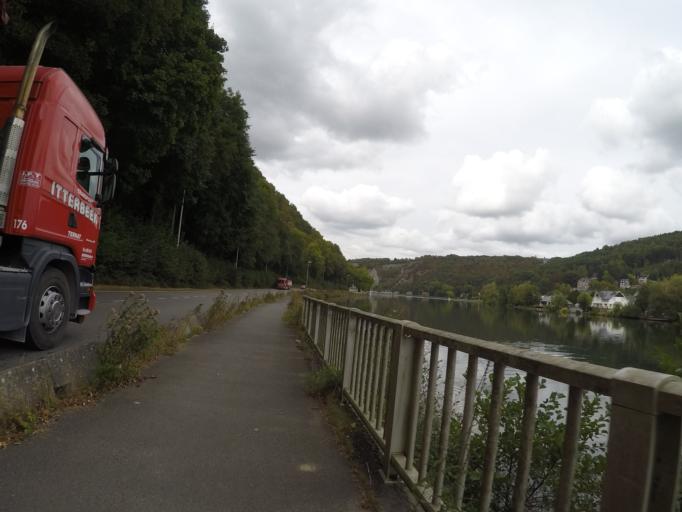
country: BE
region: Wallonia
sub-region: Province de Namur
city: Yvoir
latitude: 50.3273
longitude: 4.8711
